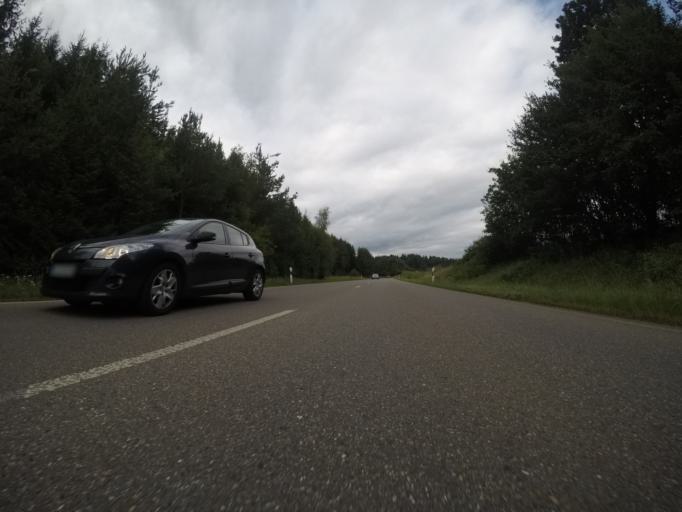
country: DE
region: Baden-Wuerttemberg
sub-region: Freiburg Region
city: Monchweiler
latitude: 48.0495
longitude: 8.4221
